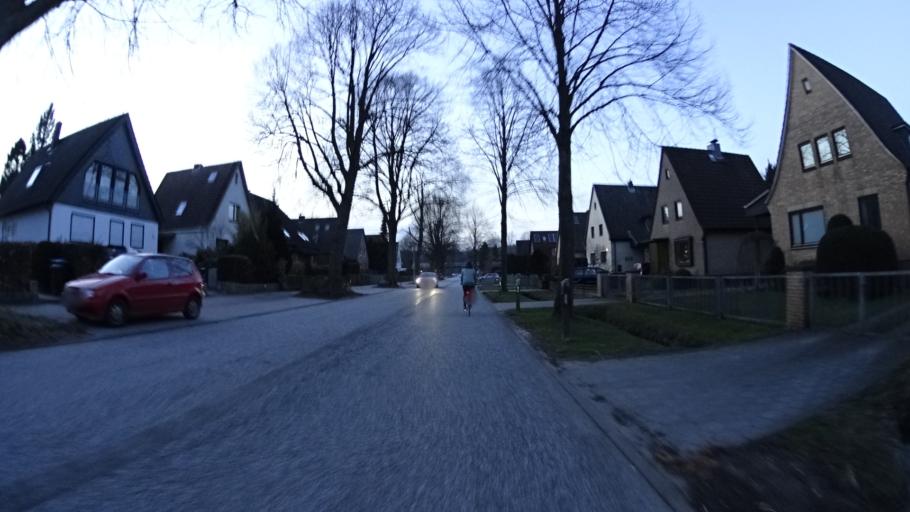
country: DE
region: Hamburg
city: Stellingen
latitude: 53.6037
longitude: 9.9300
